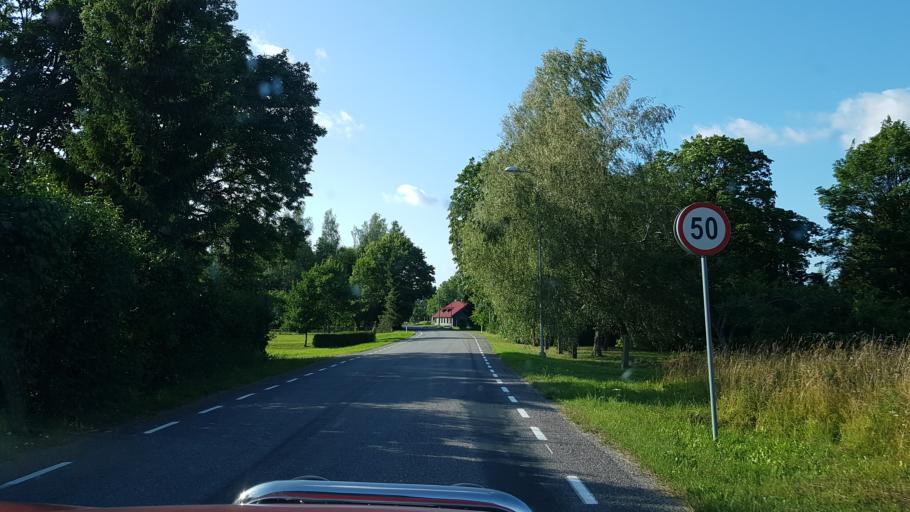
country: EE
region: Jaervamaa
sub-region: Jaerva-Jaani vald
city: Jarva-Jaani
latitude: 59.1165
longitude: 25.6641
